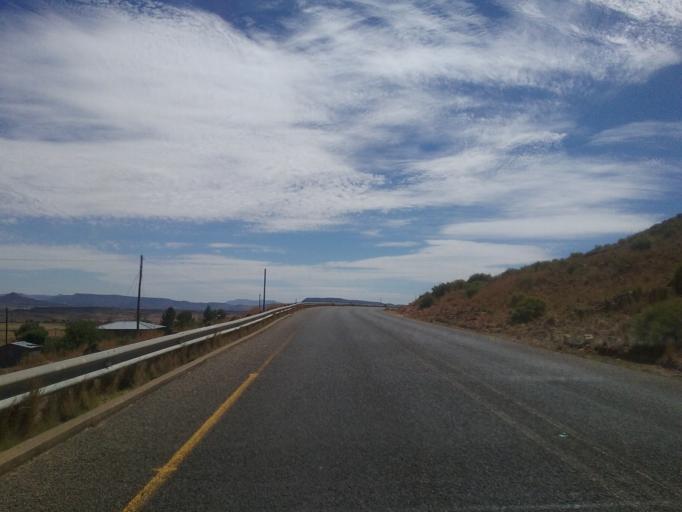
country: LS
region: Mohale's Hoek District
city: Mohale's Hoek
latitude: -30.1902
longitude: 27.4164
